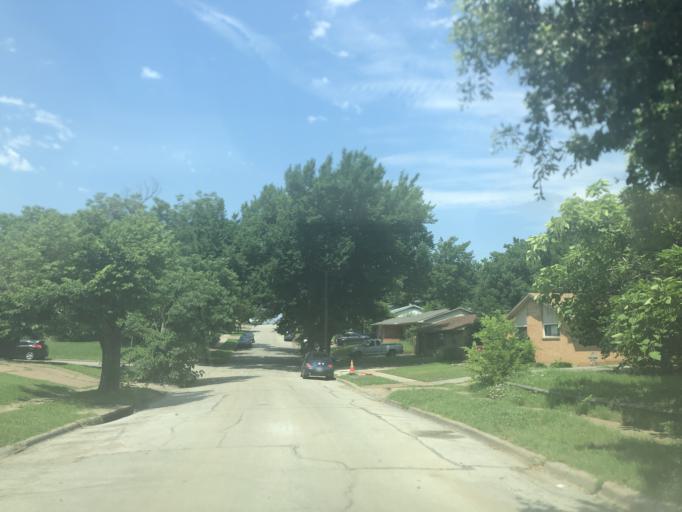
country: US
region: Texas
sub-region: Dallas County
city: Grand Prairie
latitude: 32.7241
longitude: -97.0118
